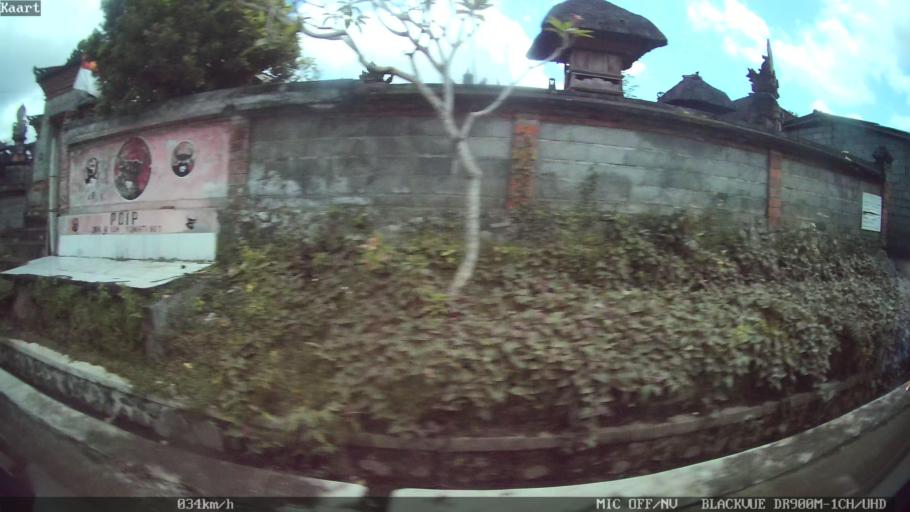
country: ID
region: Bali
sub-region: Kabupaten Gianyar
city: Ubud
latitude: -8.5422
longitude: 115.2800
